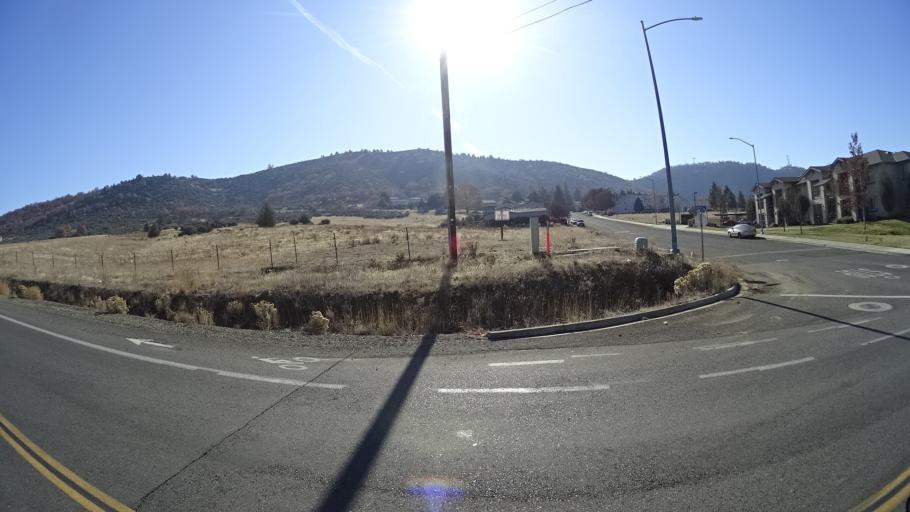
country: US
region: California
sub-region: Siskiyou County
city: Yreka
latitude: 41.7348
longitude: -122.6245
